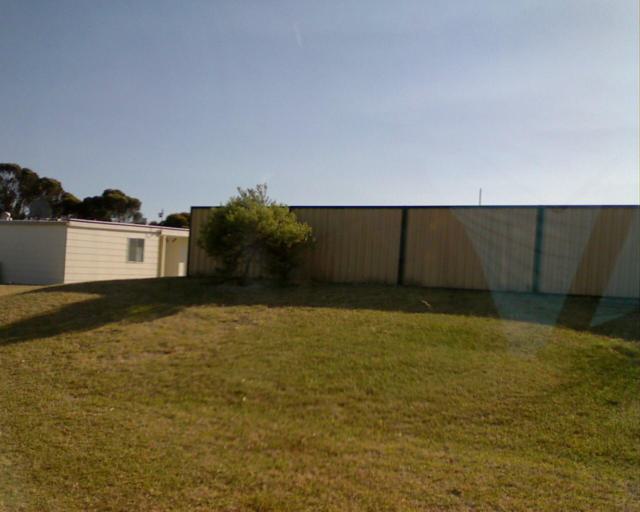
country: AU
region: Western Australia
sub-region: Dandaragan
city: Jurien Bay
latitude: -30.0664
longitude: 114.9725
